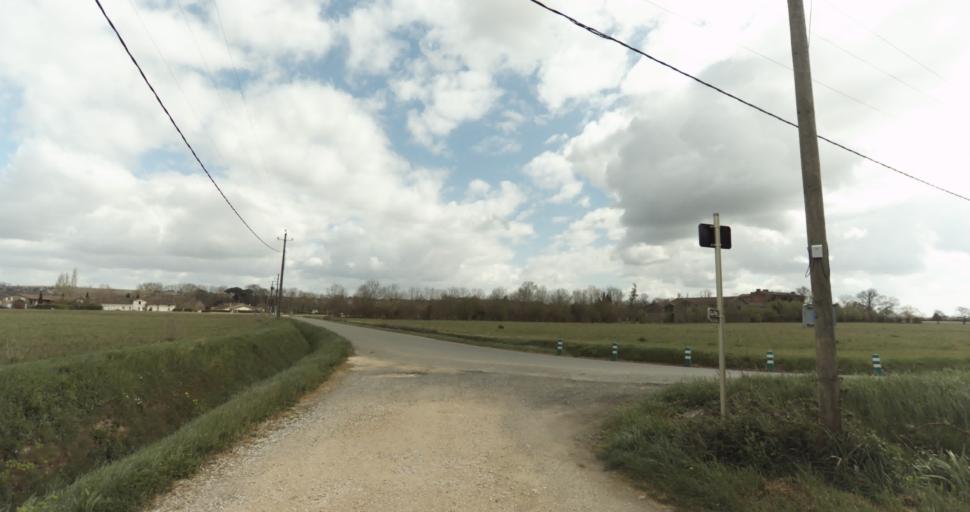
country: FR
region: Midi-Pyrenees
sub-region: Departement de la Haute-Garonne
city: Auterive
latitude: 43.3400
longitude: 1.4708
